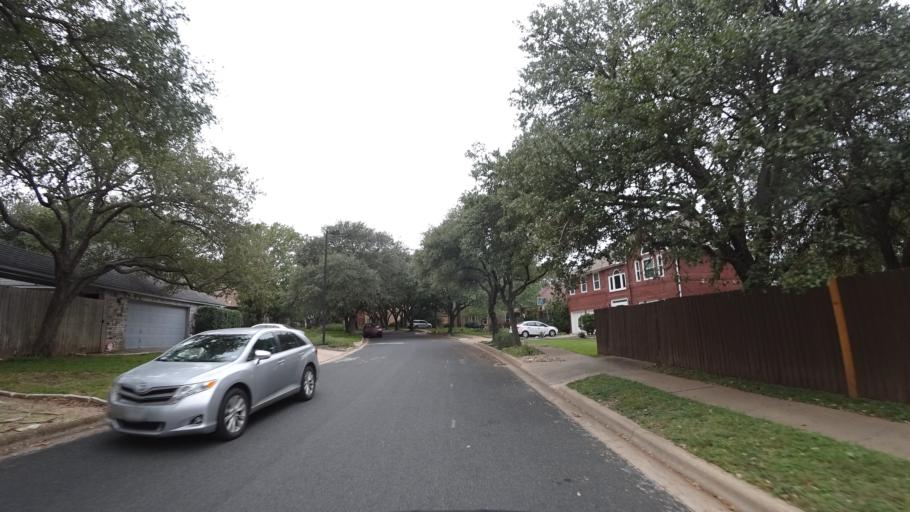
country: US
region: Texas
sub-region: Travis County
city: Shady Hollow
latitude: 30.1940
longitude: -97.8895
